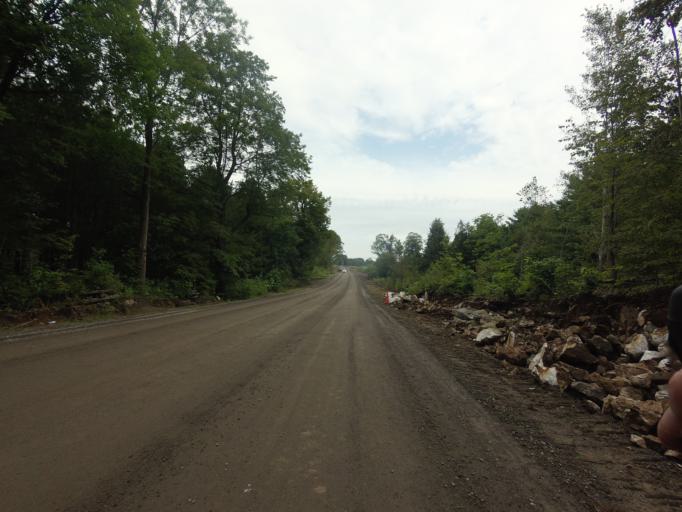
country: CA
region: Ontario
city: Kingston
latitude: 44.5800
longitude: -76.6337
